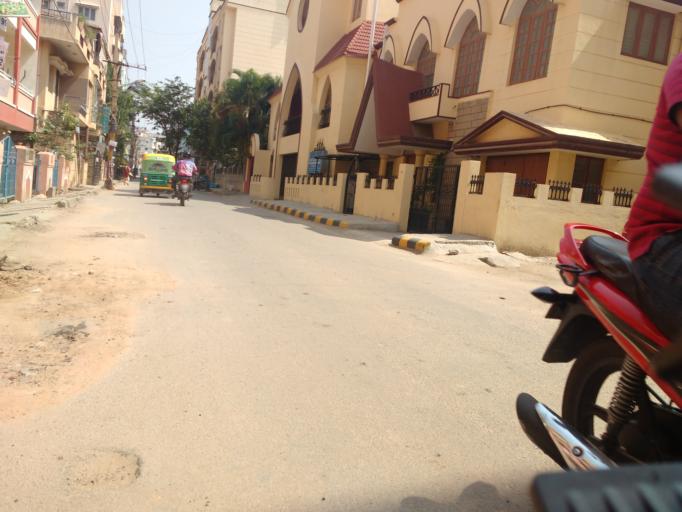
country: IN
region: Karnataka
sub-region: Bangalore Urban
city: Bangalore
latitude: 12.9911
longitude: 77.6685
